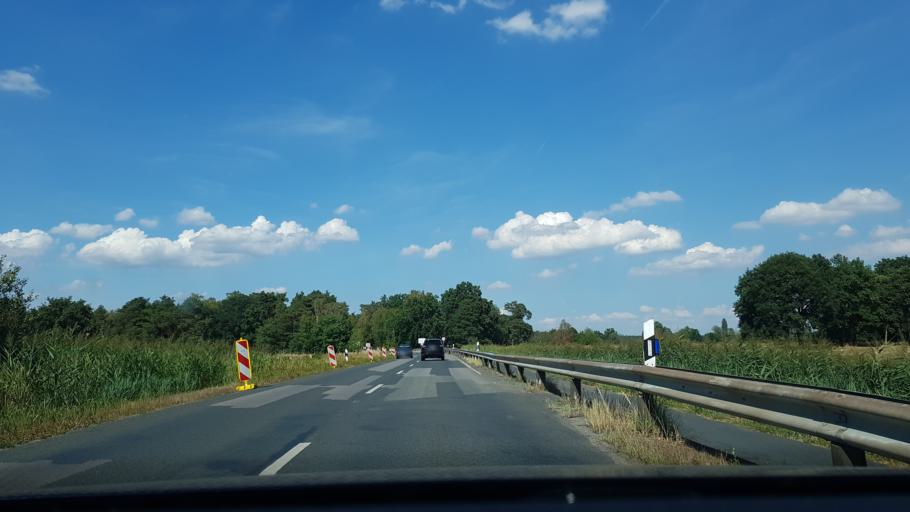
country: DE
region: Lower Saxony
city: Isenbuttel
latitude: 52.4429
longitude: 10.6067
